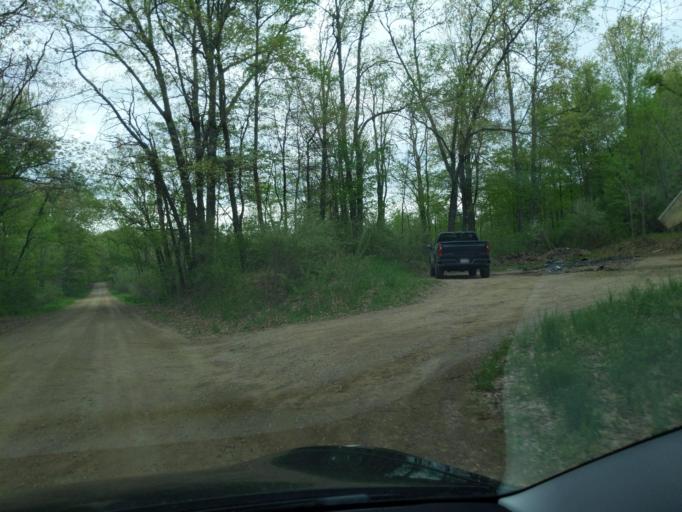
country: US
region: Michigan
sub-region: Ingham County
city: Stockbridge
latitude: 42.5175
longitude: -84.2888
